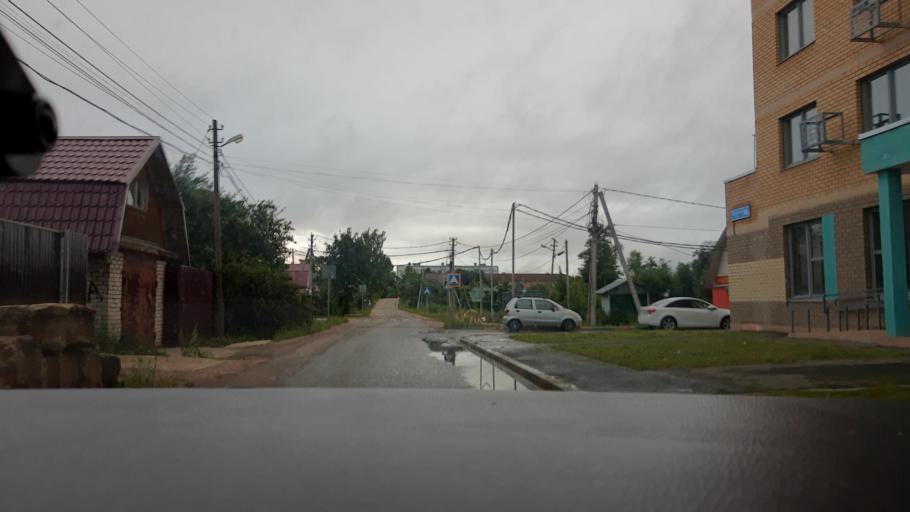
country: RU
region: Moskovskaya
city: Nekrasovskiy
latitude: 56.0945
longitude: 37.4984
